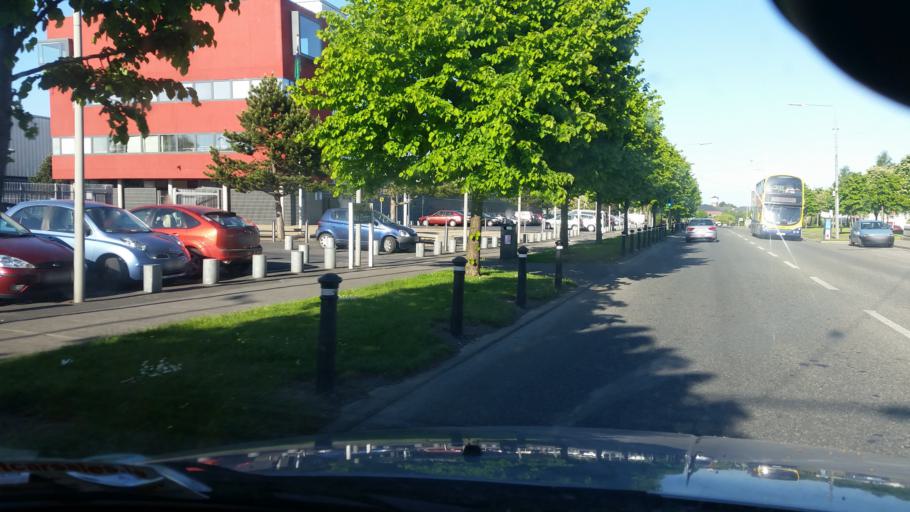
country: IE
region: Leinster
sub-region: Dublin City
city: Finglas
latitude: 53.3898
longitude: -6.3064
